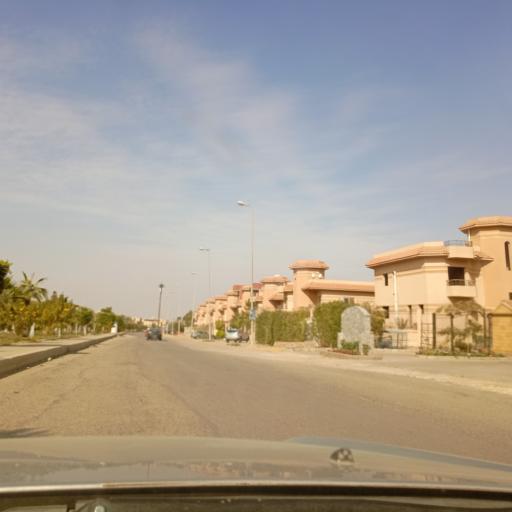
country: EG
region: Muhafazat al Qalyubiyah
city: Al Khankah
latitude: 30.0502
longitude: 31.4852
